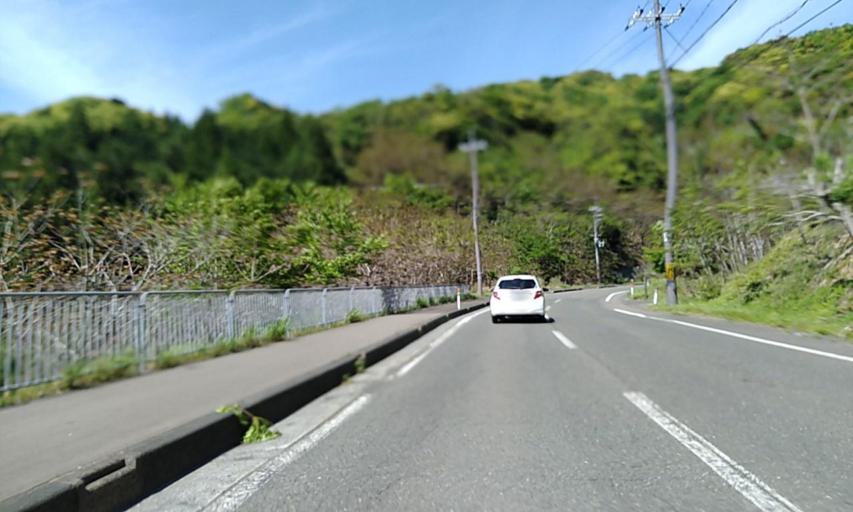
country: JP
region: Fukui
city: Obama
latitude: 35.5251
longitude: 135.8010
